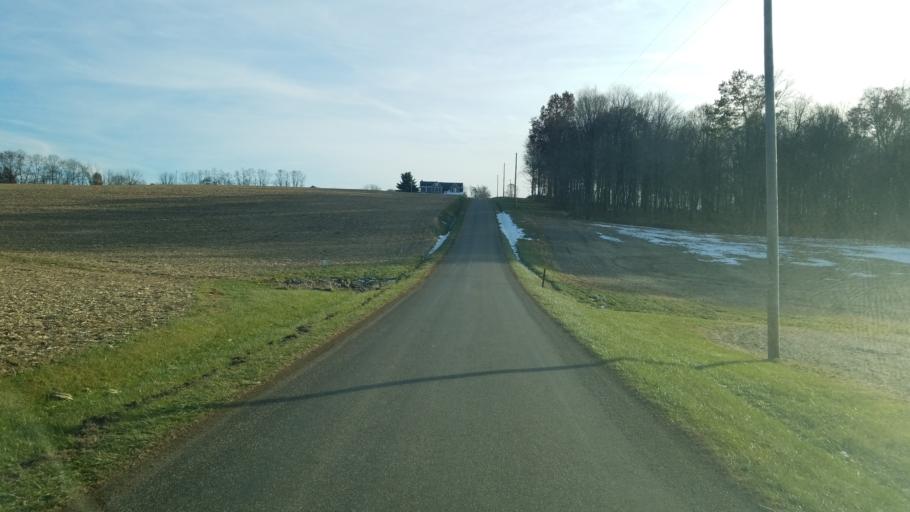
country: US
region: Ohio
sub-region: Ashland County
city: Ashland
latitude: 40.7581
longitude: -82.2883
